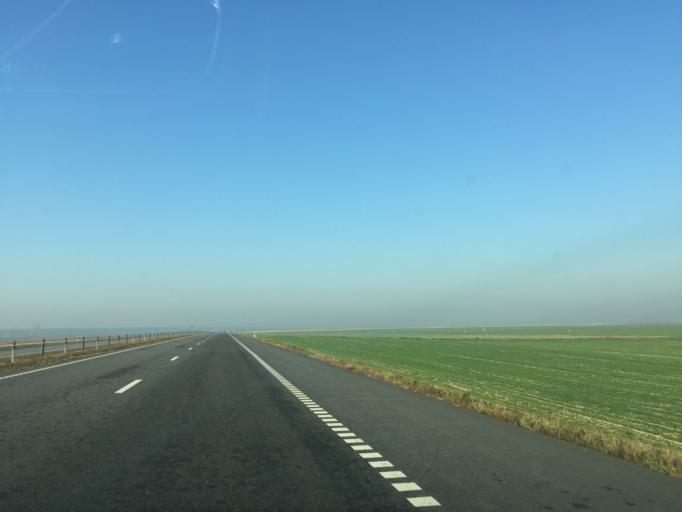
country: BY
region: Gomel
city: Kastsyukowka
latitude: 52.4881
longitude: 30.8008
